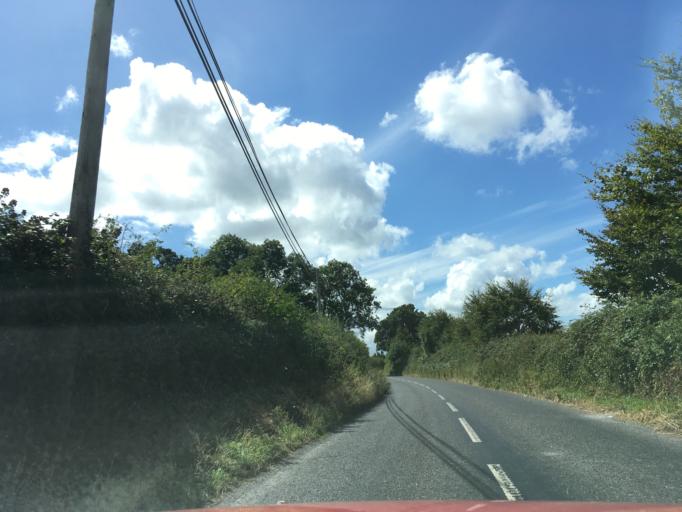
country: IE
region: Munster
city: Cahir
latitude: 52.3468
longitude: -7.9407
